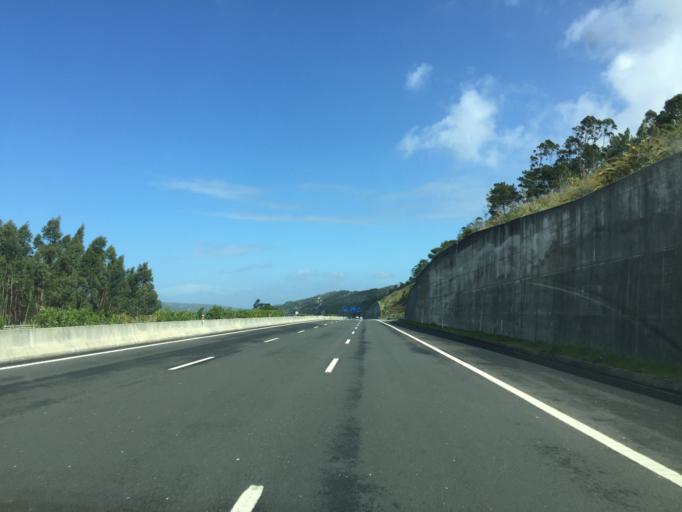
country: PT
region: Leiria
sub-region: Caldas da Rainha
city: Caldas da Rainha
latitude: 39.4879
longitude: -9.0962
